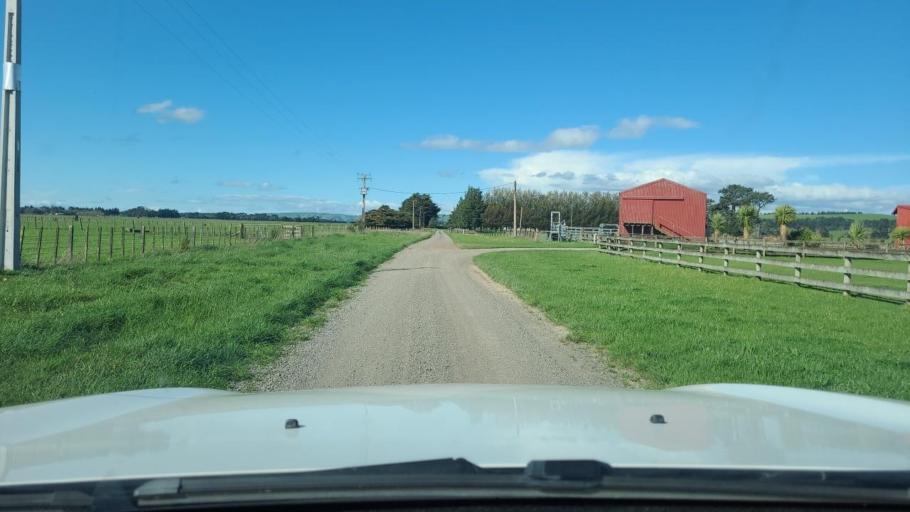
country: NZ
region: Wellington
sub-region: South Wairarapa District
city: Waipawa
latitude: -41.1858
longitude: 175.3667
